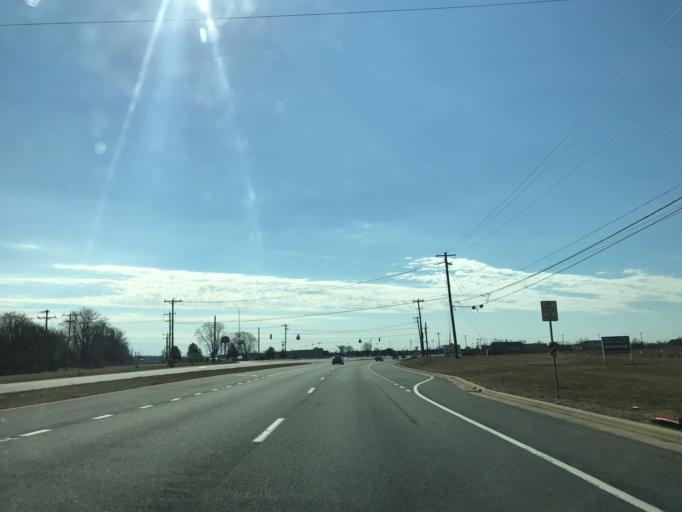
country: US
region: Delaware
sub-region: New Castle County
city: Middletown
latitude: 39.4561
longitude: -75.7229
